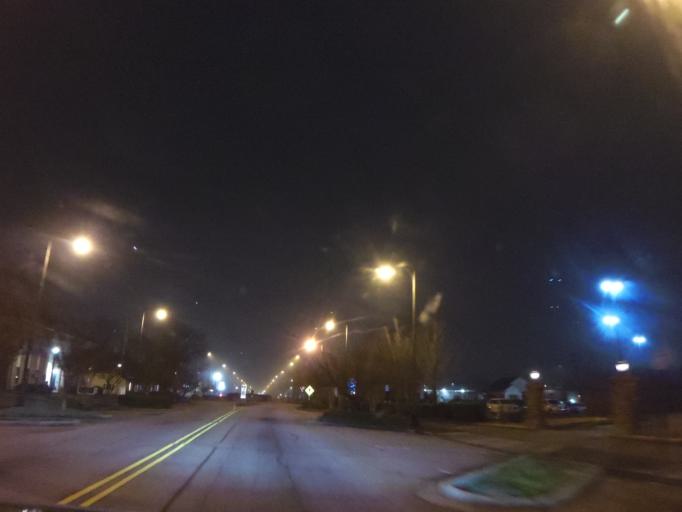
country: US
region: North Carolina
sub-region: Cumberland County
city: Fayetteville
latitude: 35.0516
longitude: -78.8754
